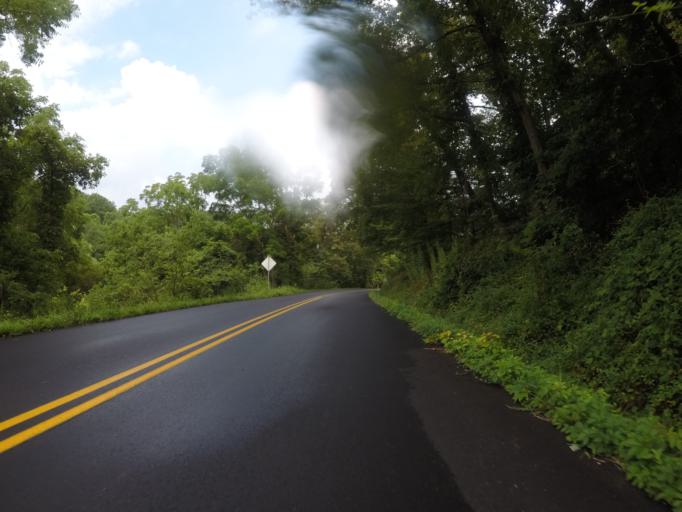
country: US
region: Kentucky
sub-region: Boyd County
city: Meads
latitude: 38.4004
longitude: -82.6562
